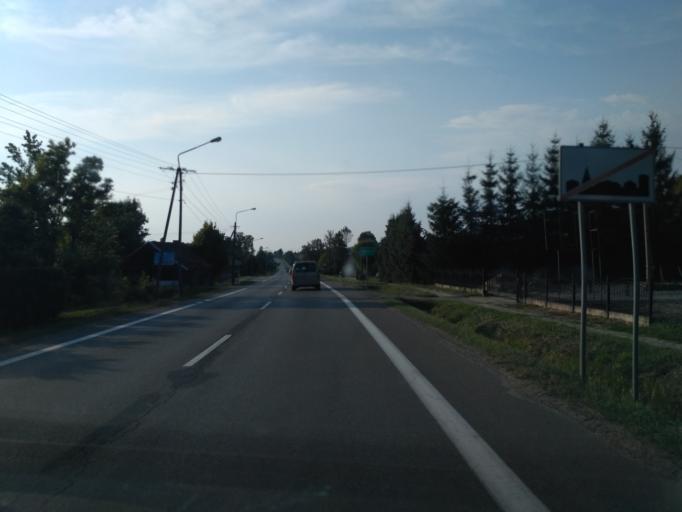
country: PL
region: Subcarpathian Voivodeship
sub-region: Powiat brzozowski
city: Stara Wies
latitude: 49.7327
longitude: 21.9985
